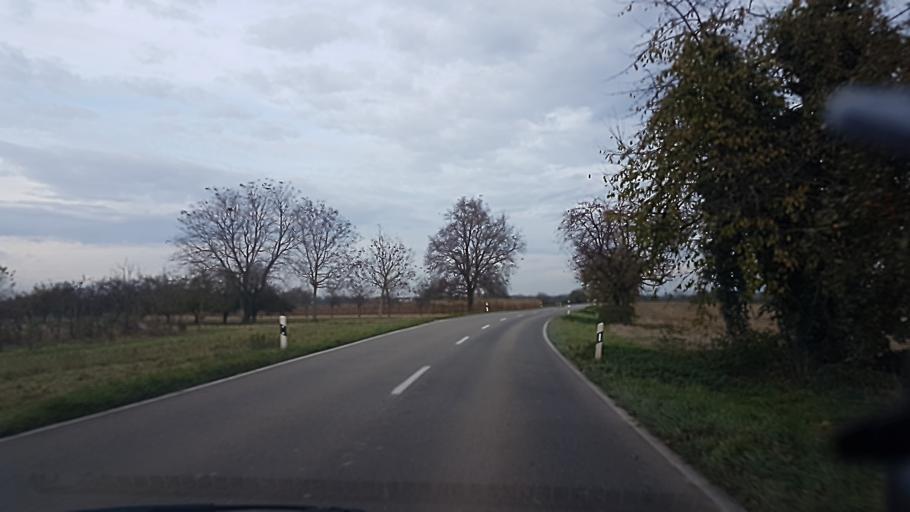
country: DE
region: Baden-Wuerttemberg
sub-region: Freiburg Region
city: Weisweil
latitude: 48.1899
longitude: 7.6727
